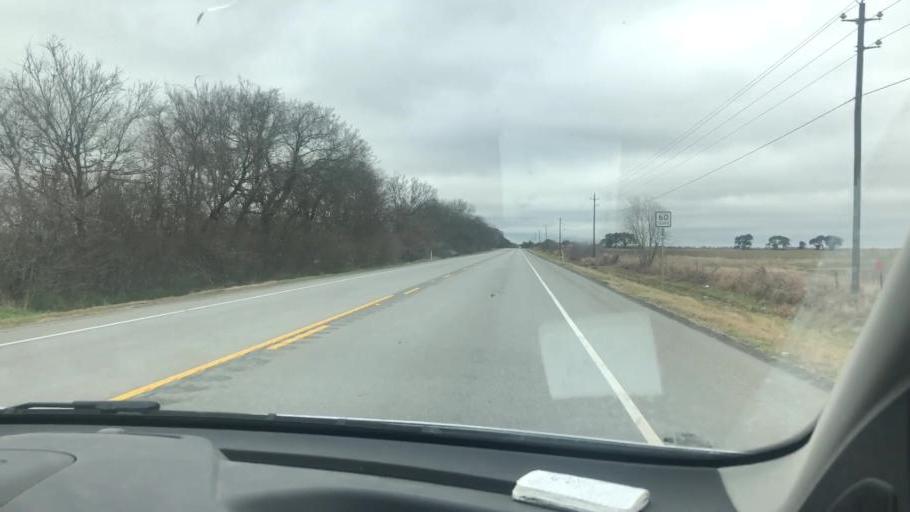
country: US
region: Texas
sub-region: Matagorda County
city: Bay City
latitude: 29.0791
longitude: -95.9732
